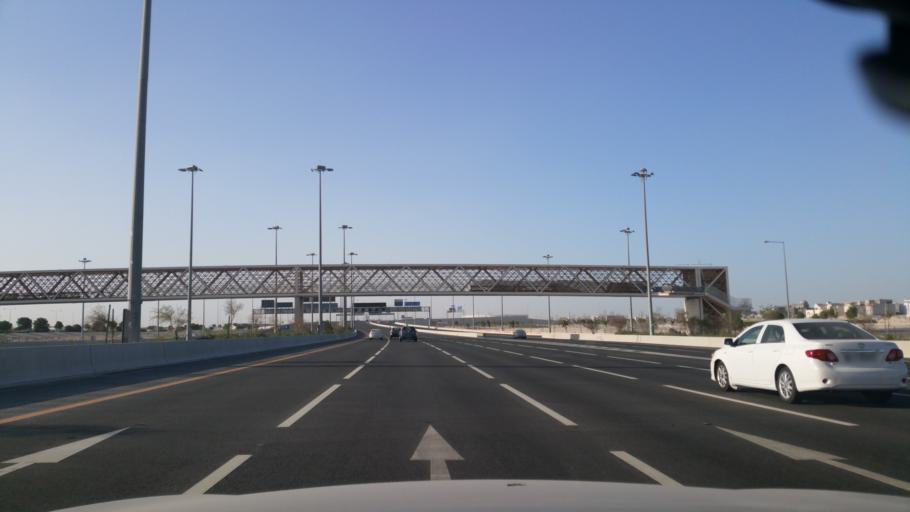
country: QA
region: Al Wakrah
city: Al Wukayr
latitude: 25.2119
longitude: 51.5388
